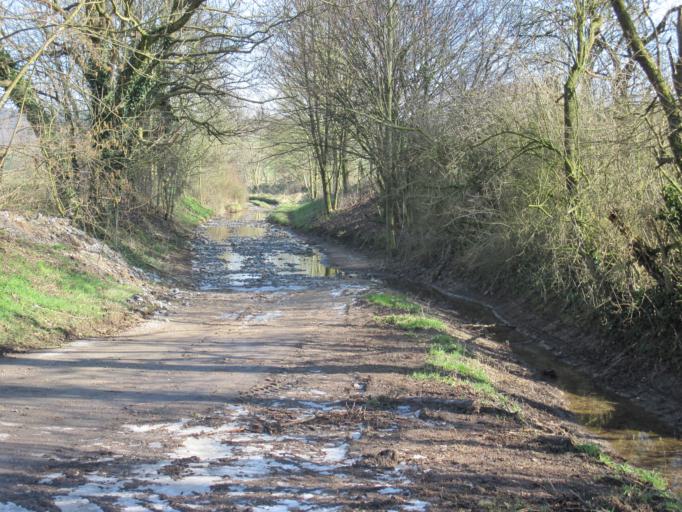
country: DE
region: North Rhine-Westphalia
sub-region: Regierungsbezirk Detmold
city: Paderborn
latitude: 51.6630
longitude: 8.7380
